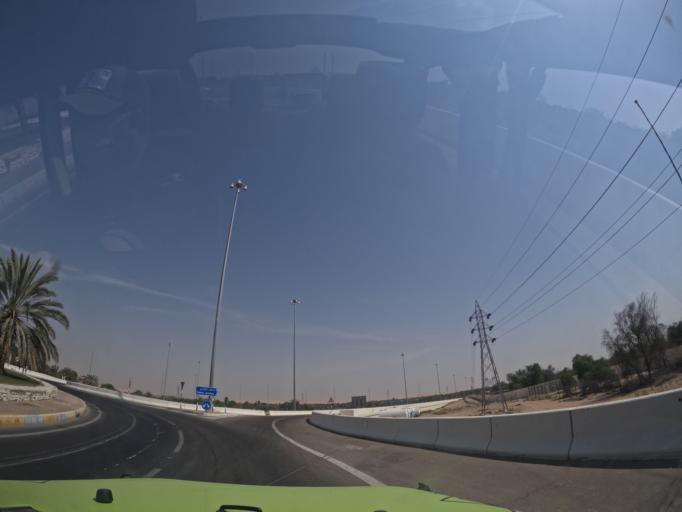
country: AE
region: Abu Dhabi
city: Al Ain
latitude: 24.1749
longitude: 55.1369
